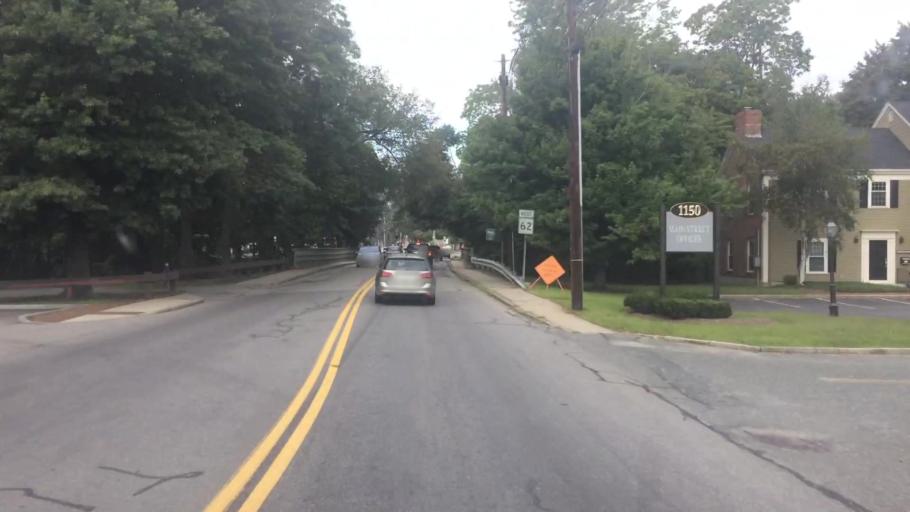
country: US
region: Massachusetts
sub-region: Middlesex County
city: West Concord
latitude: 42.4562
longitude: -71.3879
